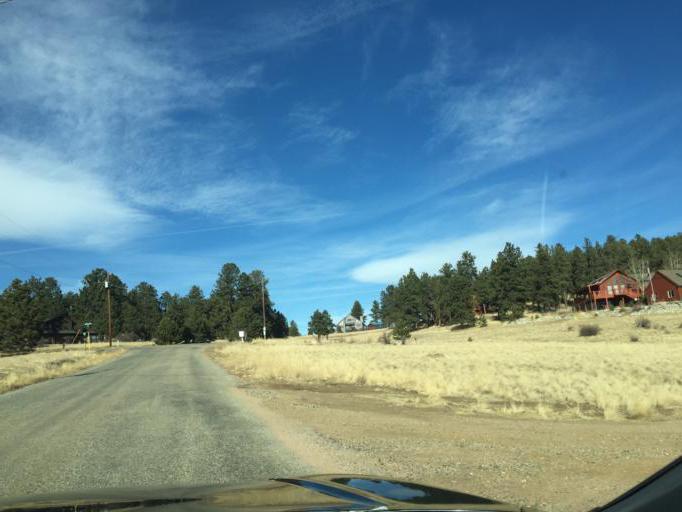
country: US
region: Colorado
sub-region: Jefferson County
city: Evergreen
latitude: 39.4424
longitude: -105.4540
